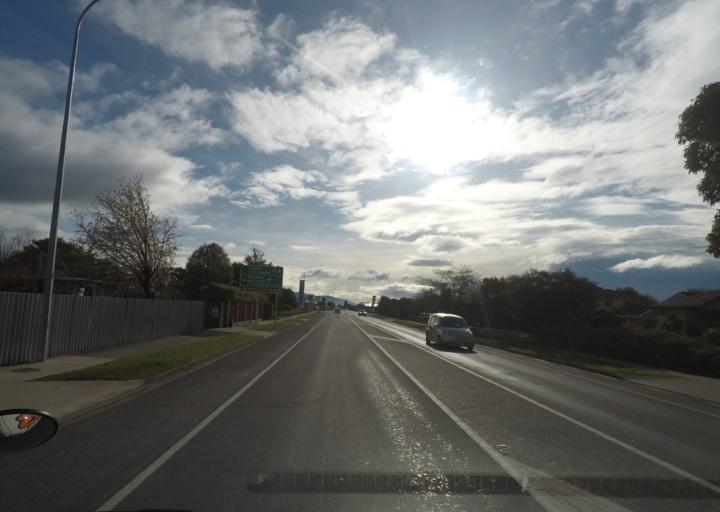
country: NZ
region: Tasman
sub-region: Tasman District
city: Motueka
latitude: -41.1259
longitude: 173.0104
